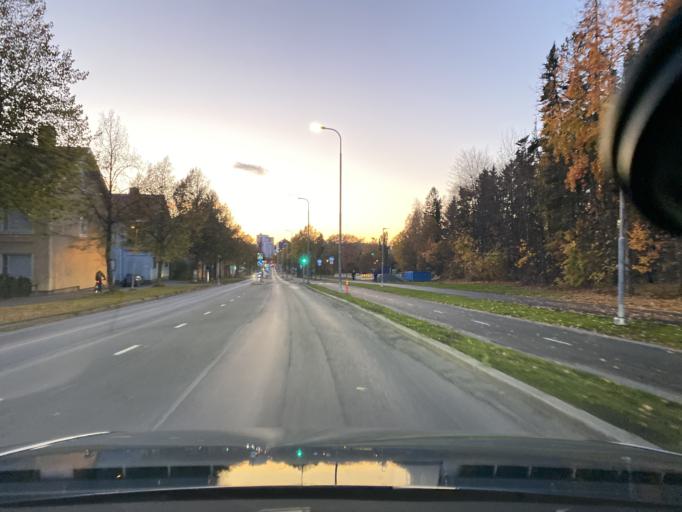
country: FI
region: Pirkanmaa
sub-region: Tampere
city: Tampere
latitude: 61.4705
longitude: 23.7373
